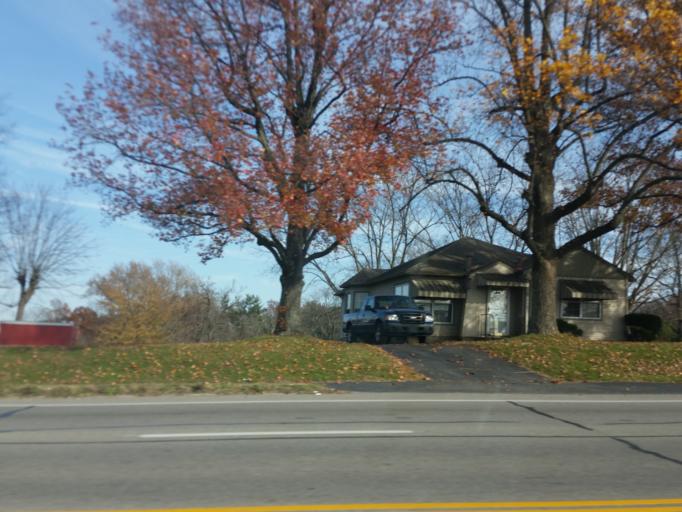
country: US
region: Kentucky
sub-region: Campbell County
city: Alexandria
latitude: 38.9755
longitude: -84.3925
